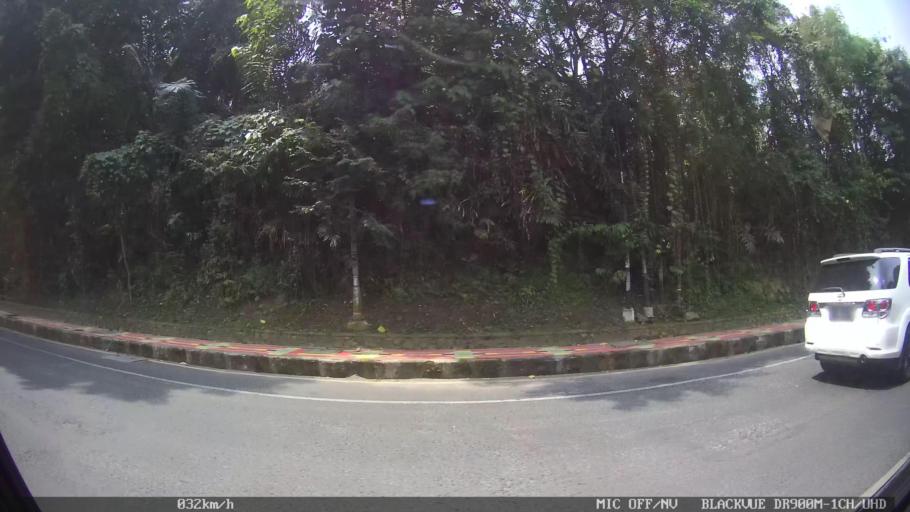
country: ID
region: Lampung
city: Bandarlampung
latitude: -5.4273
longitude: 105.2591
